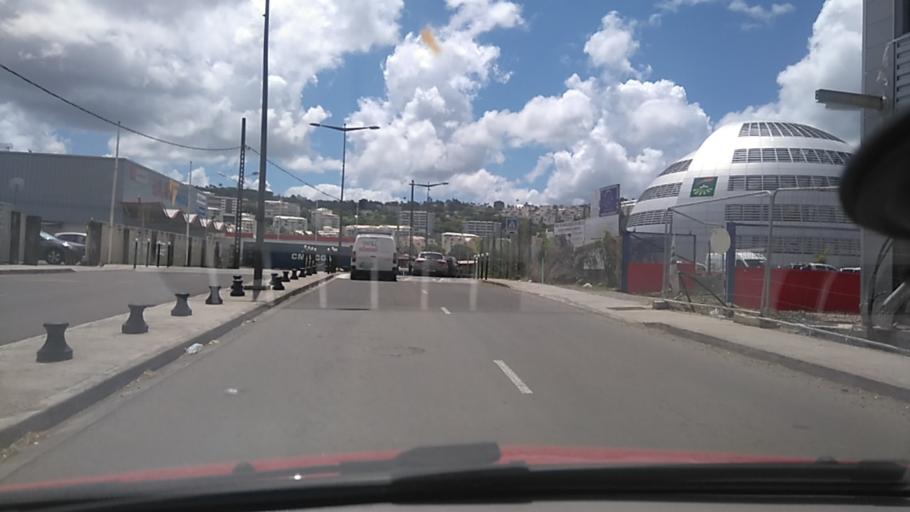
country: MQ
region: Martinique
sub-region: Martinique
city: Fort-de-France
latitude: 14.6116
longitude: -61.0522
